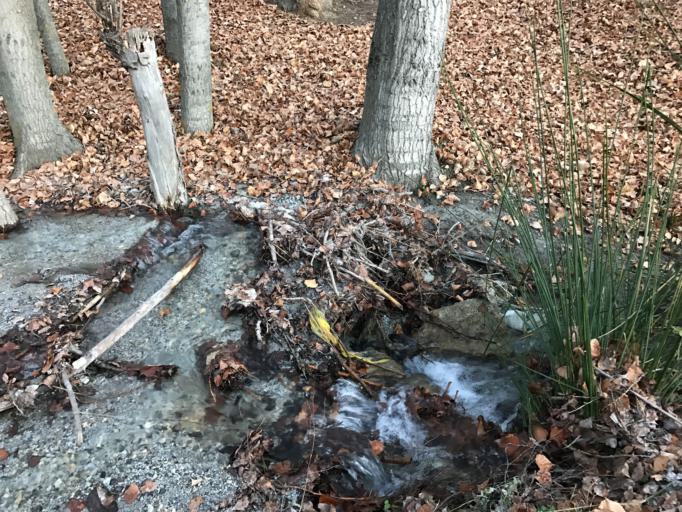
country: ES
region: Andalusia
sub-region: Provincia de Granada
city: Beas de Granada
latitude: 37.2279
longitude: -3.4754
